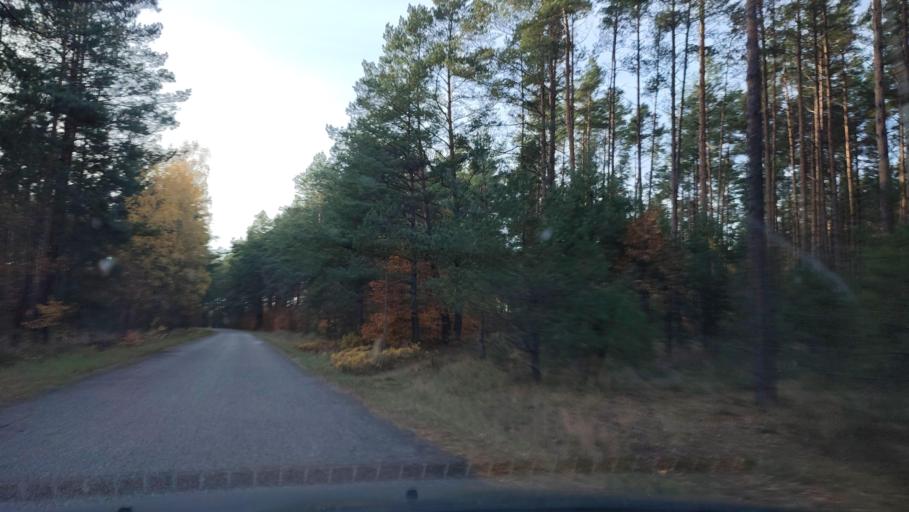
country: PL
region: Masovian Voivodeship
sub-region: Powiat przasnyski
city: Chorzele
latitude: 53.3311
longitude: 20.7328
